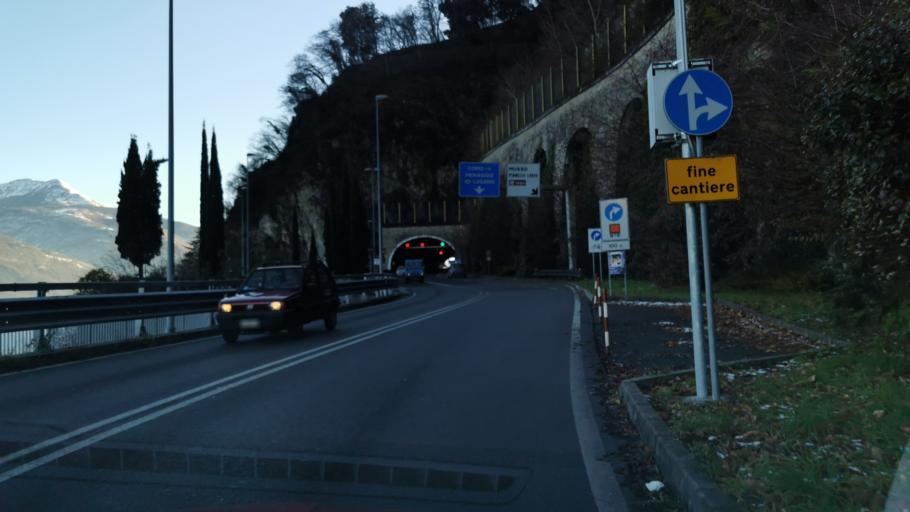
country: IT
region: Lombardy
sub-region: Provincia di Como
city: Dongo
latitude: 46.1211
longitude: 9.2797
